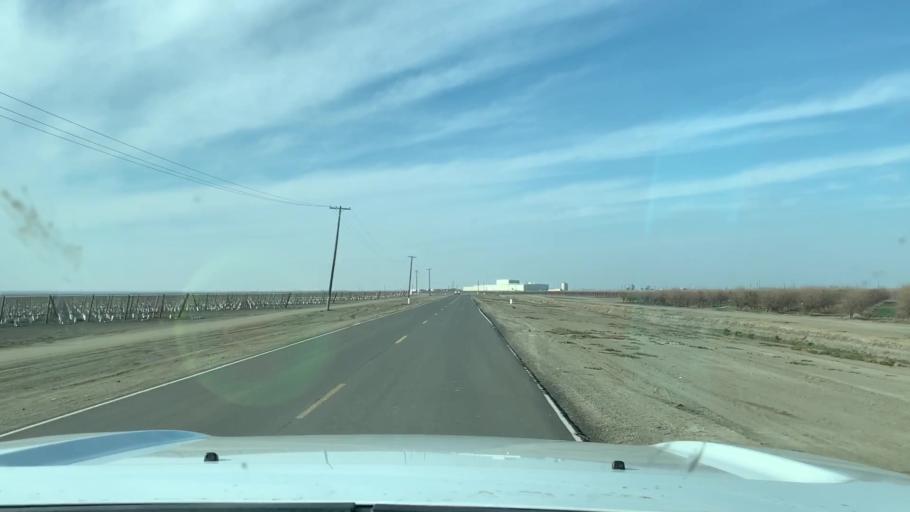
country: US
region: California
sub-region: Kern County
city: Buttonwillow
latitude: 35.4905
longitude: -119.5988
